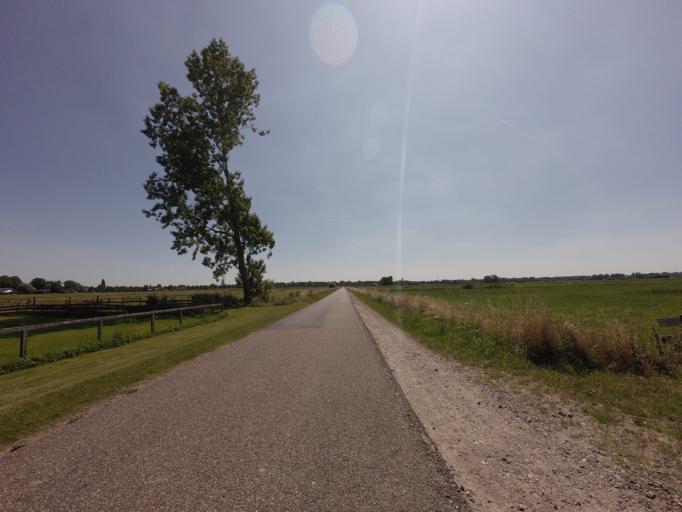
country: NL
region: Utrecht
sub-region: Stichtse Vecht
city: Maarssen
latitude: 52.1586
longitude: 5.0692
